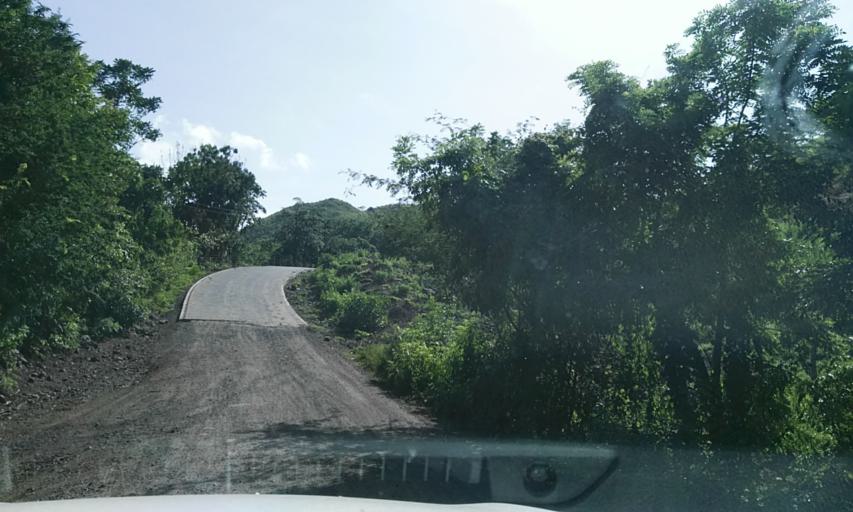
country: NI
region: Matagalpa
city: Terrabona
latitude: 12.7545
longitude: -85.9871
